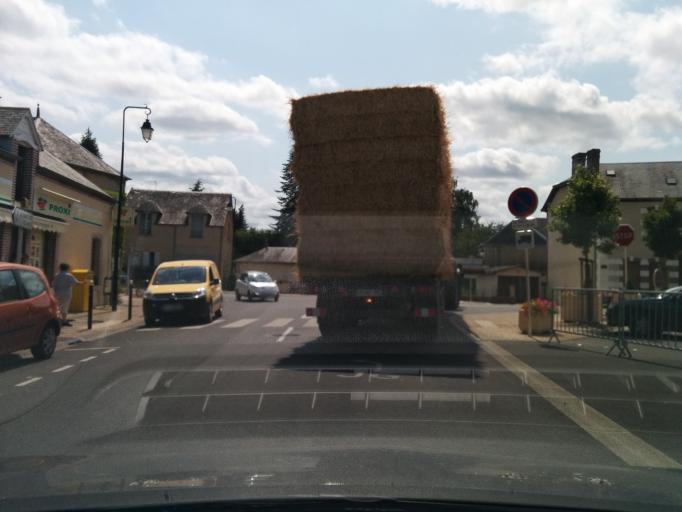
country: FR
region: Centre
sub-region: Departement du Cher
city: Henrichemont
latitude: 47.3442
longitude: 2.4882
